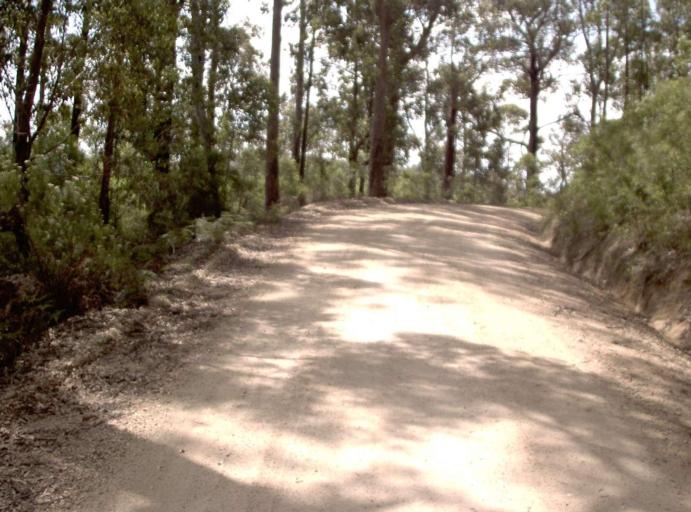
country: AU
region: Victoria
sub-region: East Gippsland
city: Lakes Entrance
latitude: -37.6108
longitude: 148.7001
